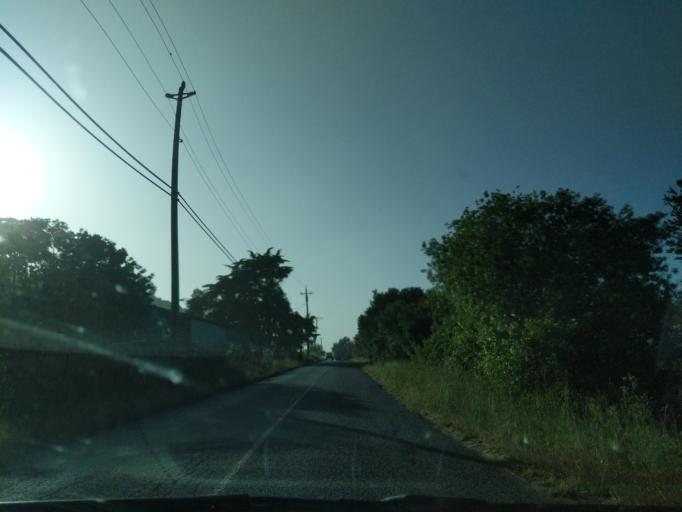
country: US
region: California
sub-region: San Benito County
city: Aromas
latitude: 36.8892
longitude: -121.6876
